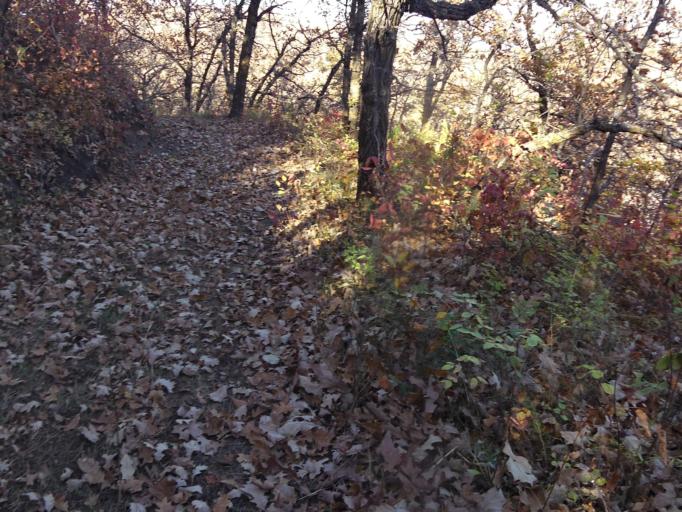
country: CA
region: Manitoba
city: Morden
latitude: 48.9464
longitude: -98.0737
